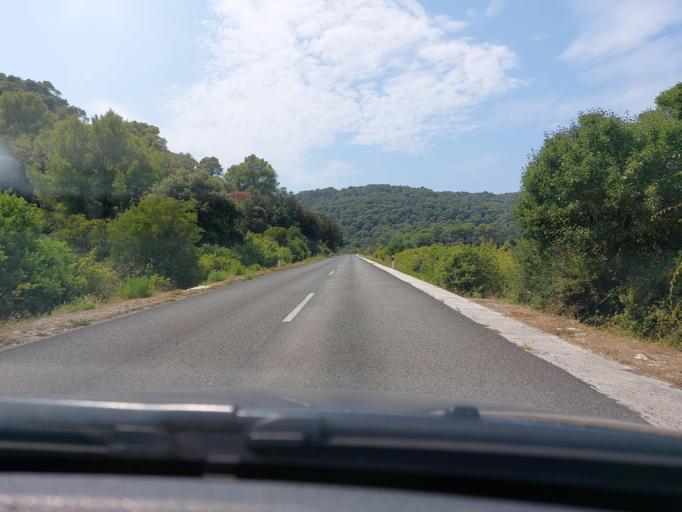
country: HR
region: Dubrovacko-Neretvanska
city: Smokvica
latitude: 42.7537
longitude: 16.8419
